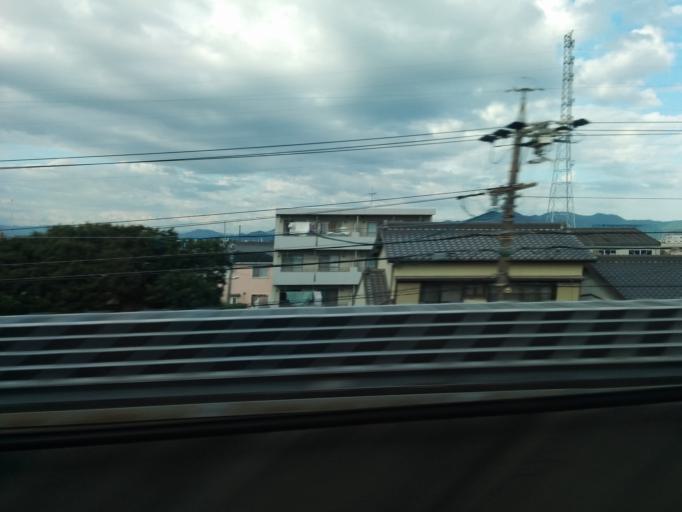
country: JP
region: Aichi
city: Toyohashi
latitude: 34.7445
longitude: 137.3957
